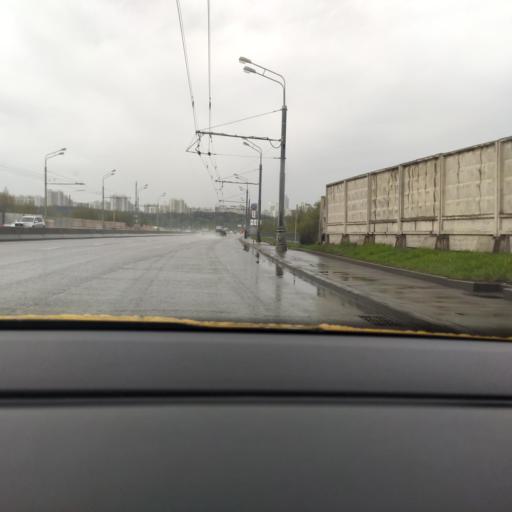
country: RU
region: Moskovskaya
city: Fili
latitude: 55.7522
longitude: 37.4543
